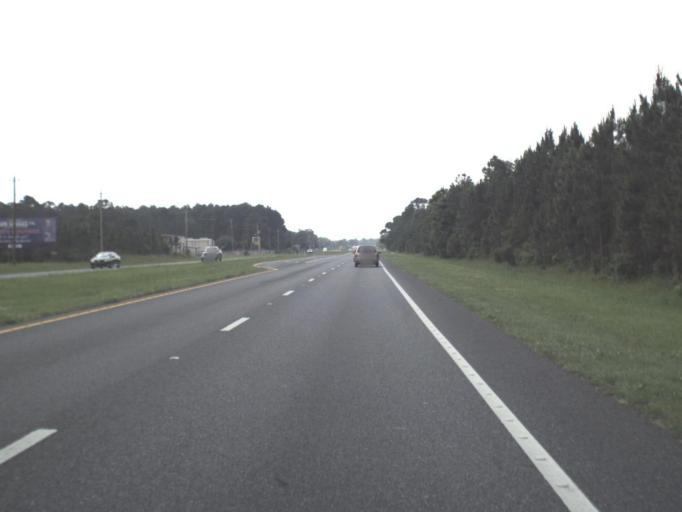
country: US
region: Florida
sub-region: Putnam County
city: Palatka
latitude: 29.6805
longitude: -81.6611
